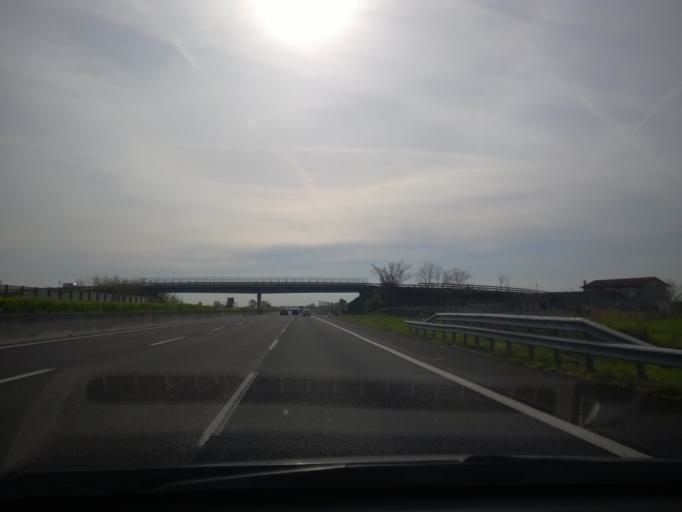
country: IT
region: Emilia-Romagna
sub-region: Forli-Cesena
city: Bagnarola
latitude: 44.1434
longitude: 12.3366
